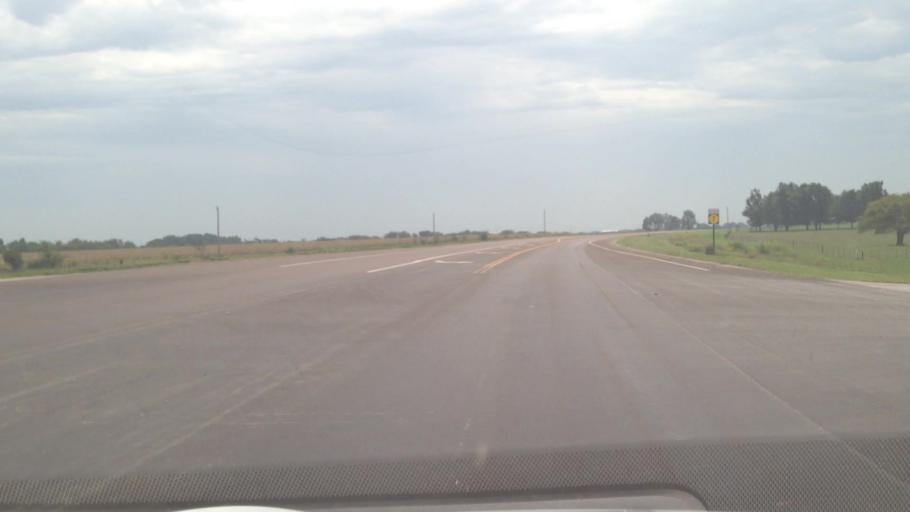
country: US
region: Kansas
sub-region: Crawford County
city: Girard
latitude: 37.4696
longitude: -94.8343
